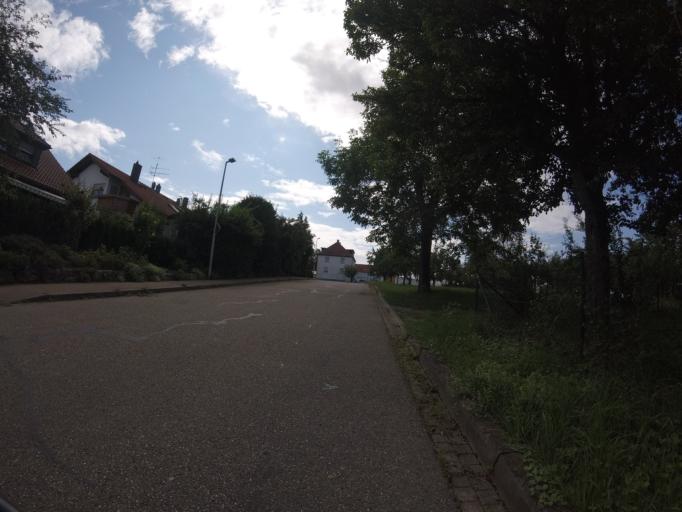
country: DE
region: Baden-Wuerttemberg
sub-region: Regierungsbezirk Stuttgart
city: Leutenbach
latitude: 48.8994
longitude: 9.4028
